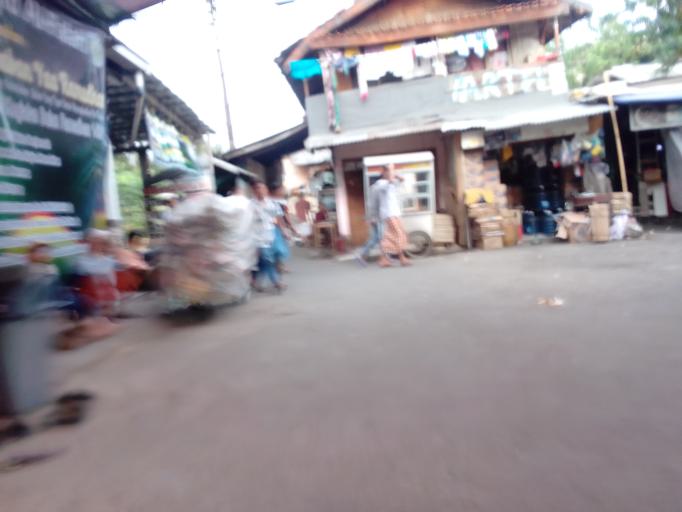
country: ID
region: Jakarta Raya
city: Jakarta
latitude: -6.1843
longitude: 106.8126
